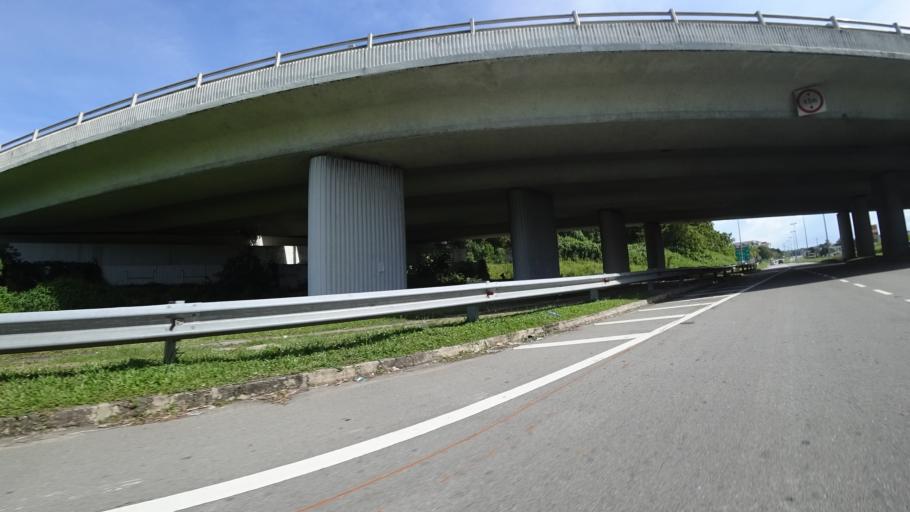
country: BN
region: Brunei and Muara
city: Bandar Seri Begawan
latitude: 4.9512
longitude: 114.8417
